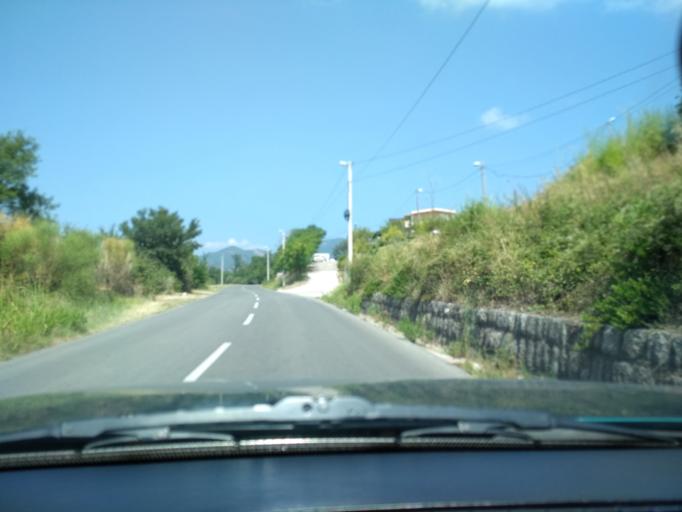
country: ME
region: Kotor
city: Kotor
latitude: 42.3933
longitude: 18.7557
